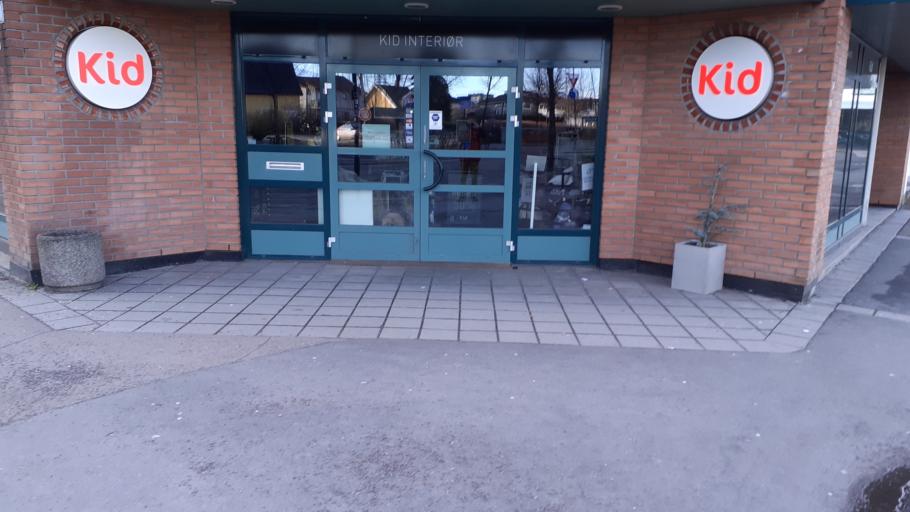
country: NO
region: Akershus
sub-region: Skedsmo
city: Lillestrom
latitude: 59.9573
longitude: 11.0512
